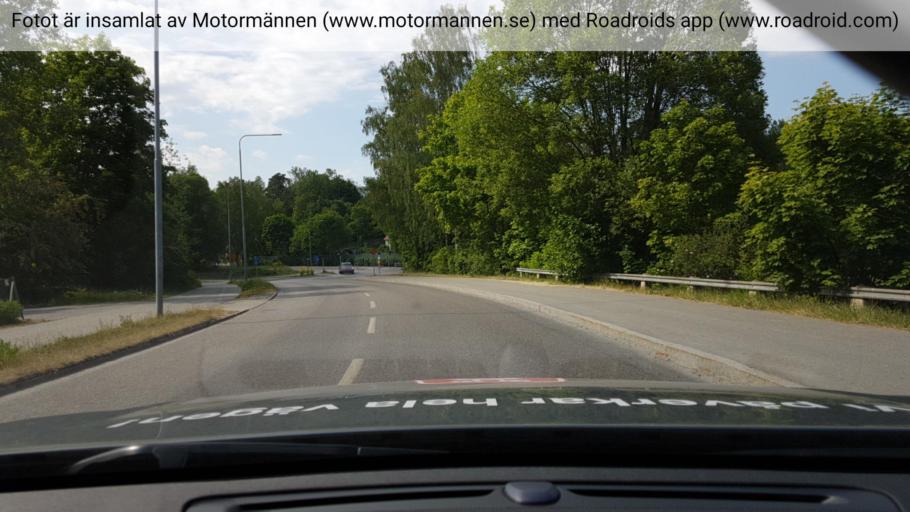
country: SE
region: Stockholm
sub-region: Lidingo
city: Lidingoe
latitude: 59.3702
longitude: 18.1293
